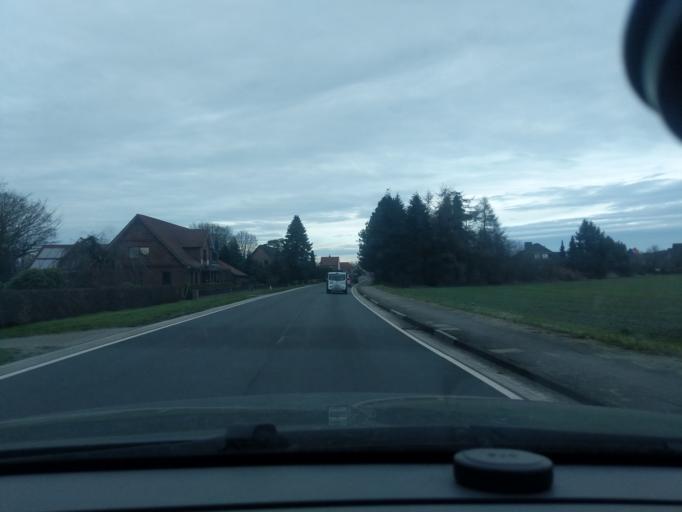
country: DE
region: Lower Saxony
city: Sauensiek
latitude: 53.3849
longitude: 9.5987
